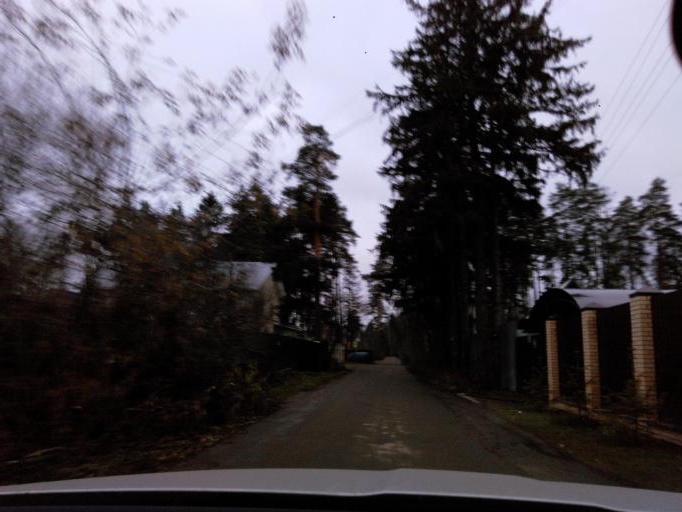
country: RU
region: Moskovskaya
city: Lozhki
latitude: 56.0501
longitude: 37.1018
